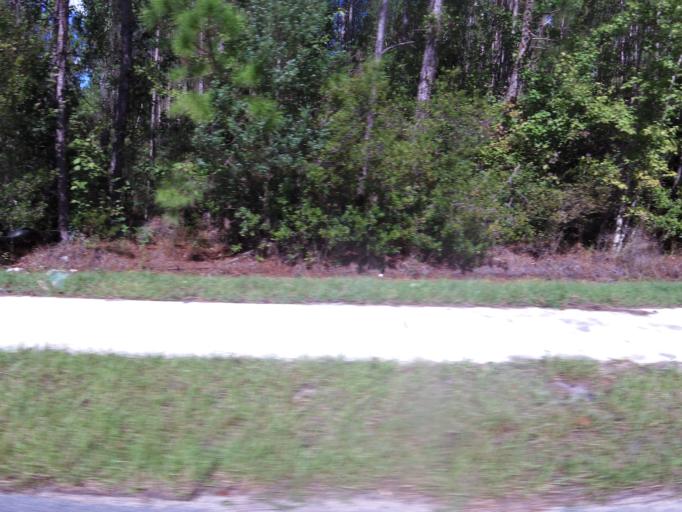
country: US
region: Florida
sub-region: Saint Johns County
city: Fruit Cove
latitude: 30.0591
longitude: -81.6333
